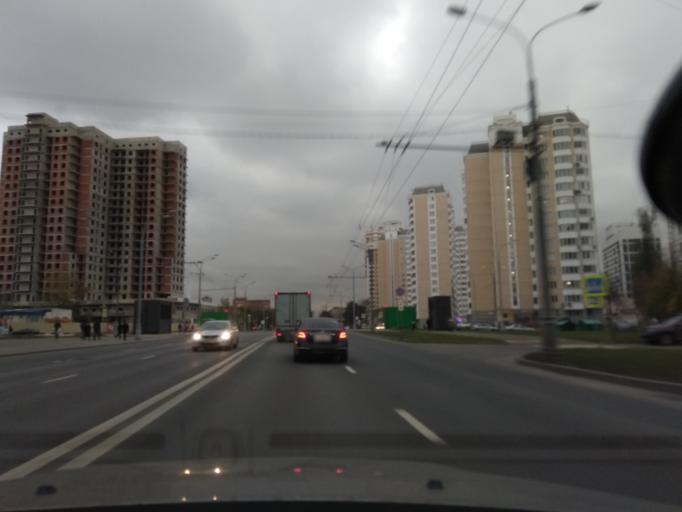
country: RU
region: Moscow
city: Novovladykino
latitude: 55.8248
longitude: 37.5848
